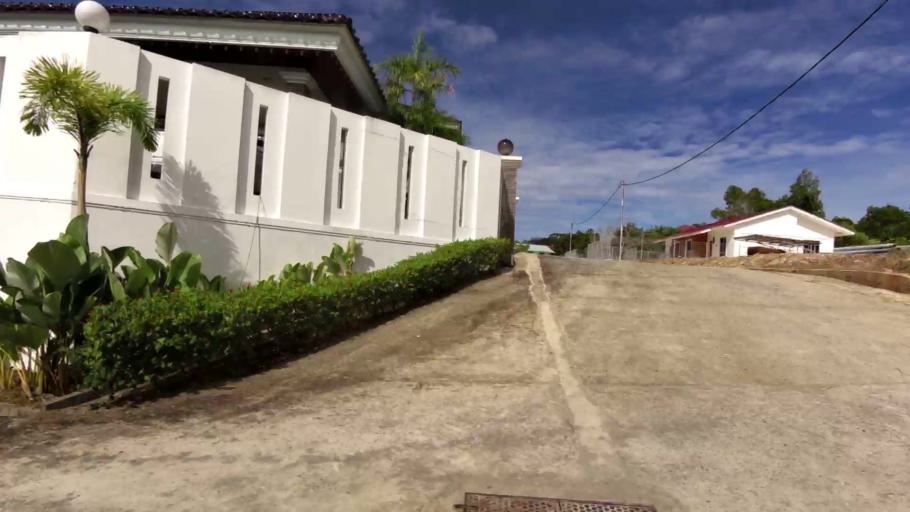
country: BN
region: Brunei and Muara
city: Bandar Seri Begawan
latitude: 4.9035
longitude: 114.9759
